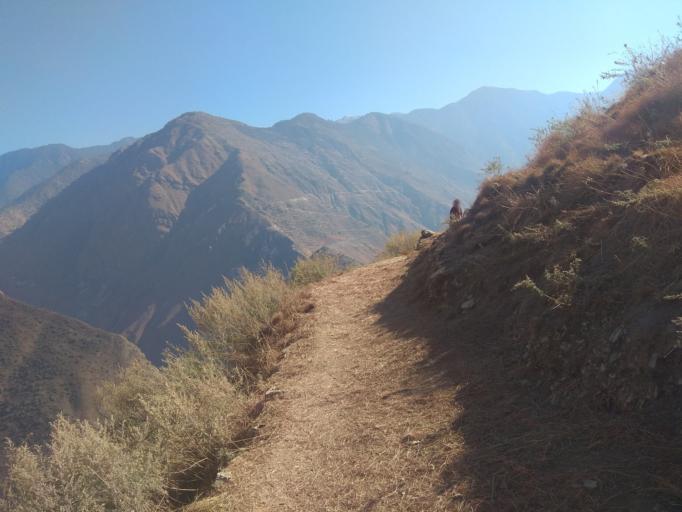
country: NP
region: Mid Western
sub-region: Karnali Zone
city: Jumla
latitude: 29.3133
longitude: 81.7463
